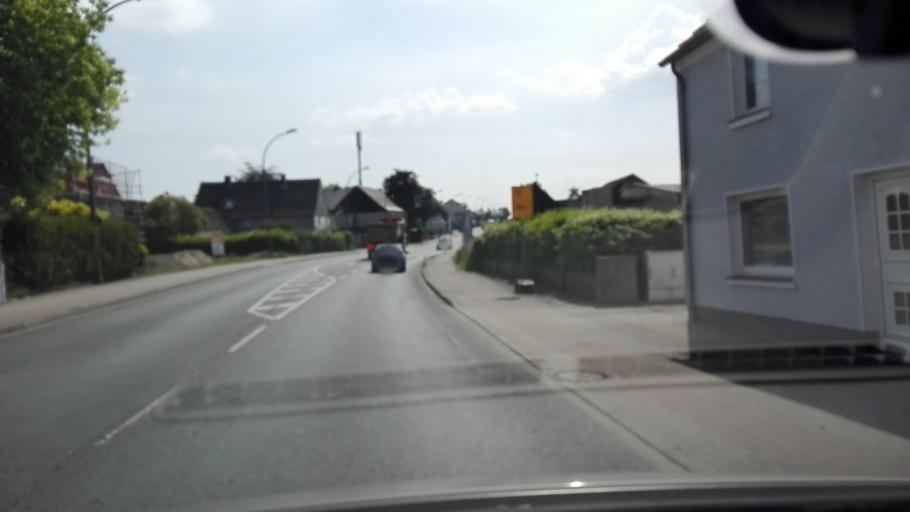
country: DE
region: North Rhine-Westphalia
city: Lanstrop
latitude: 51.6050
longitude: 7.5872
